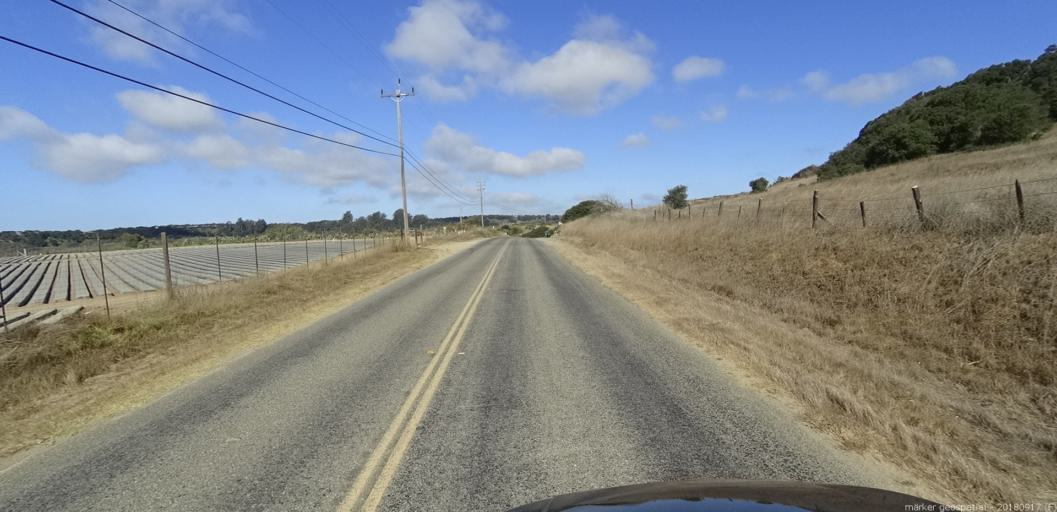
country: US
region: California
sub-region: Monterey County
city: Elkhorn
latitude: 36.8451
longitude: -121.7474
